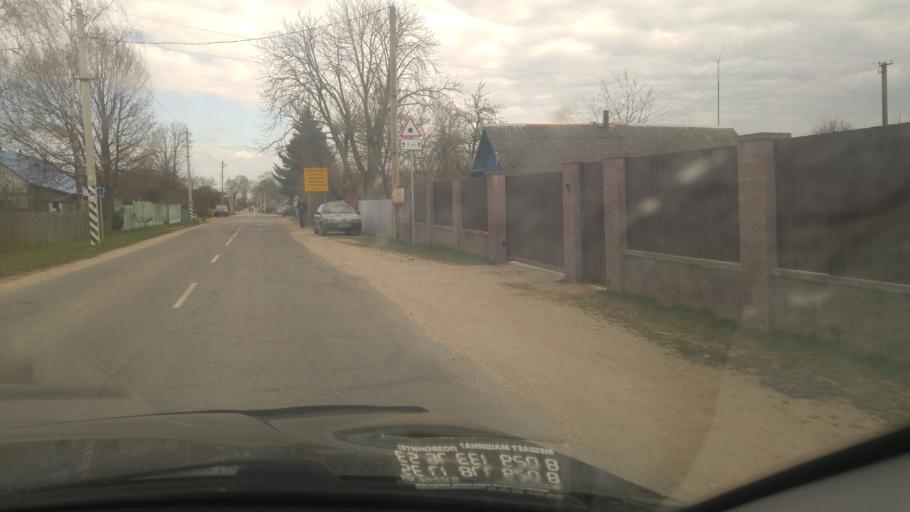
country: BY
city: Michanovichi
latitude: 53.6634
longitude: 27.7657
